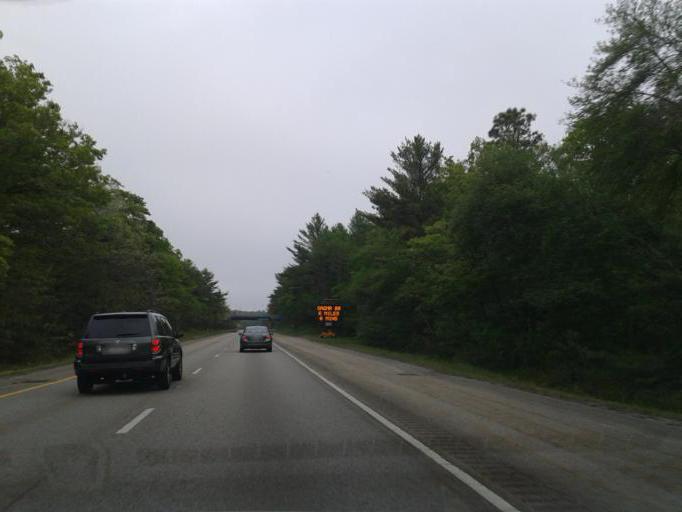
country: US
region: Massachusetts
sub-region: Plymouth County
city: White Island Shores
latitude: 41.8609
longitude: -70.5879
